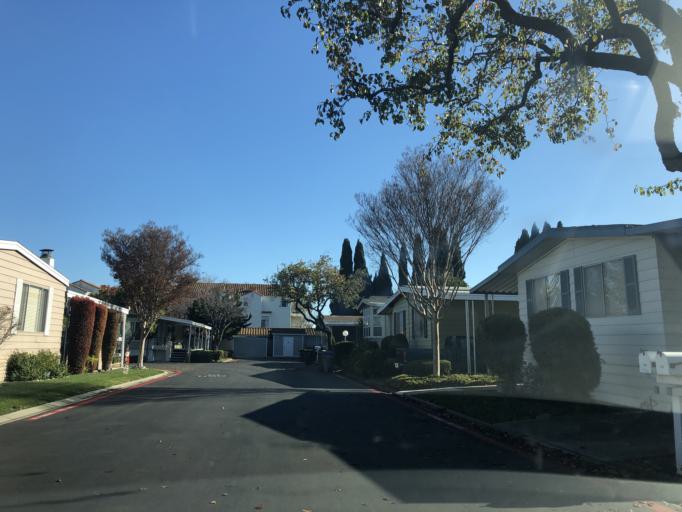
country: US
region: California
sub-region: Santa Clara County
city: Sunnyvale
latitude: 37.3992
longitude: -122.0203
